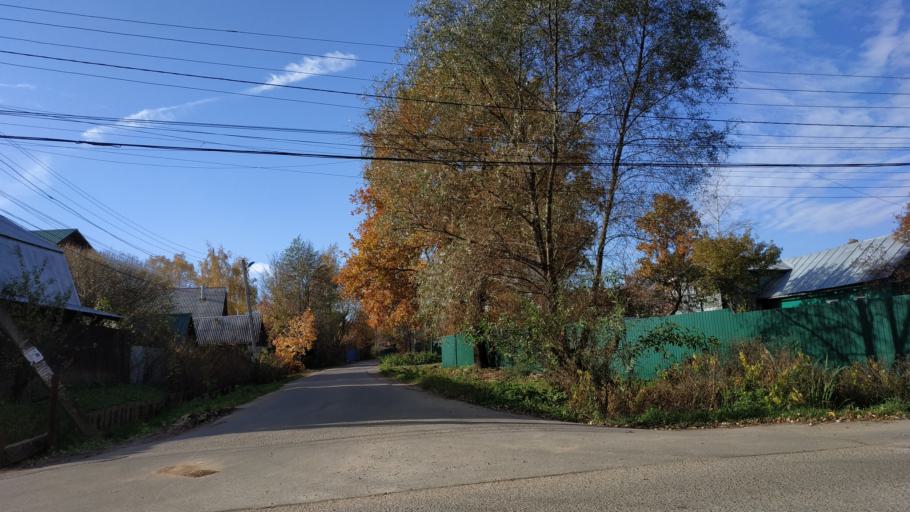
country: RU
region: Moskovskaya
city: Sheremet'yevskiy
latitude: 55.9843
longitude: 37.4887
